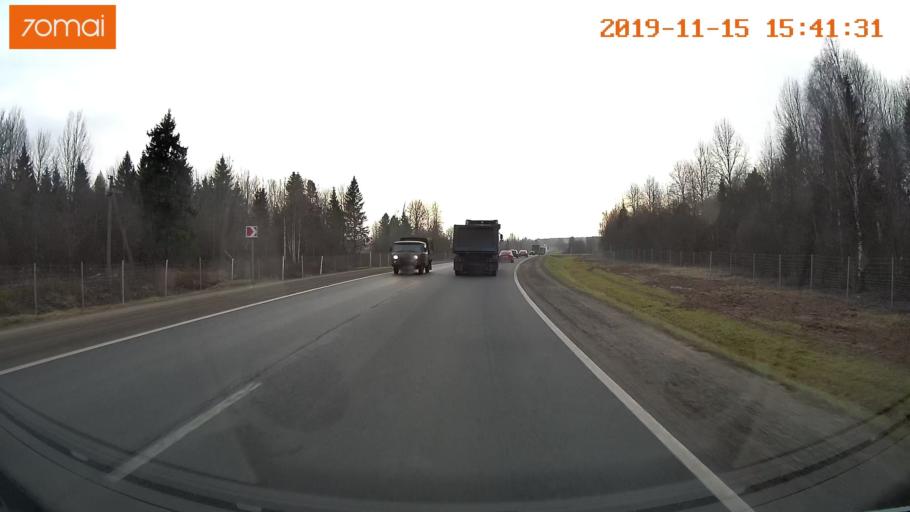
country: RU
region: Jaroslavl
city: Danilov
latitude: 57.9998
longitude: 40.0475
